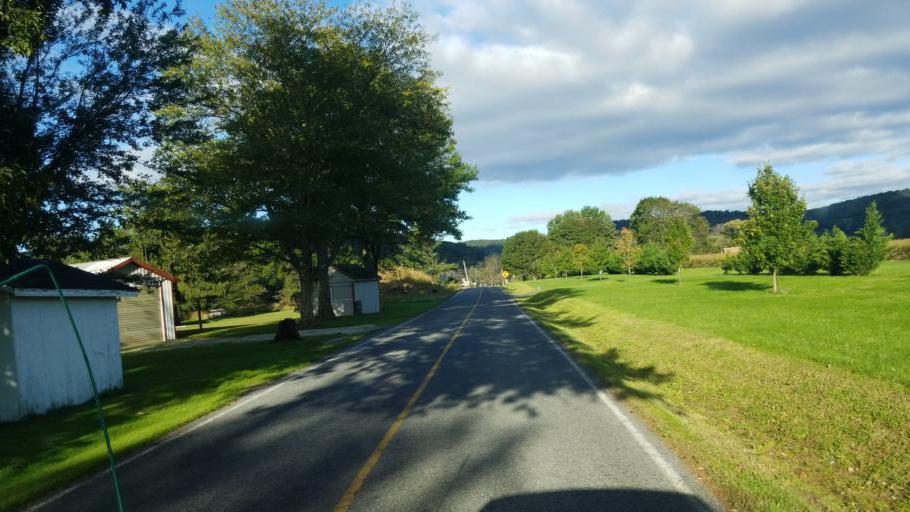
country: US
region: Pennsylvania
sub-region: Adams County
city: Biglerville
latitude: 39.8887
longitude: -77.3455
